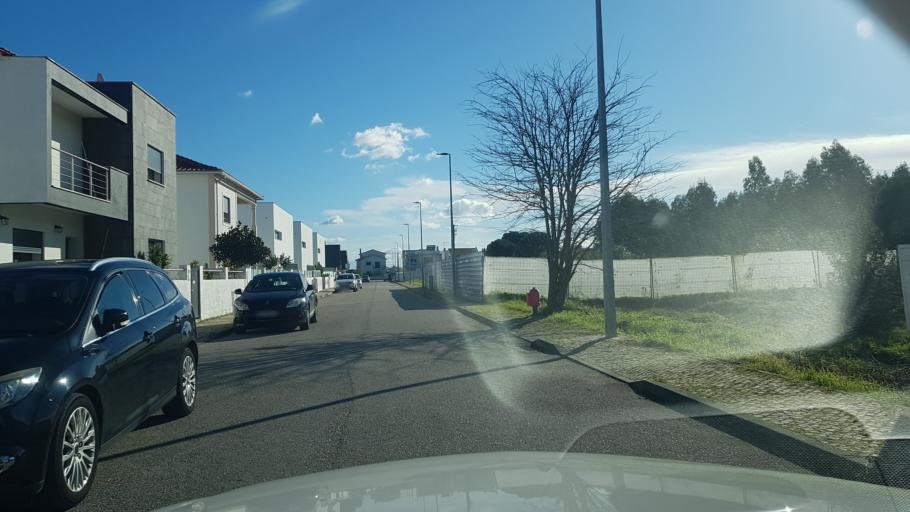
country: PT
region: Santarem
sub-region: Entroncamento
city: Entroncamento
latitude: 39.4795
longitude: -8.4784
